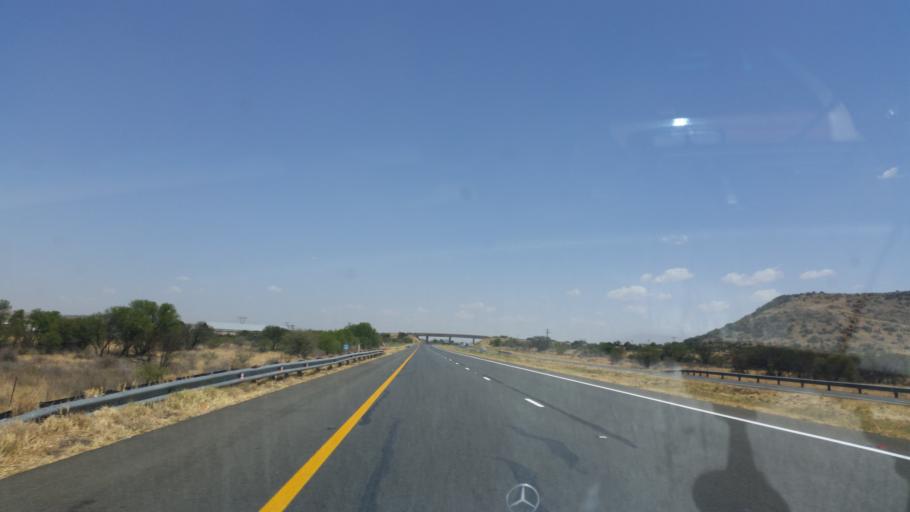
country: ZA
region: Orange Free State
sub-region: Mangaung Metropolitan Municipality
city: Bloemfontein
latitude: -28.9496
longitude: 26.3972
